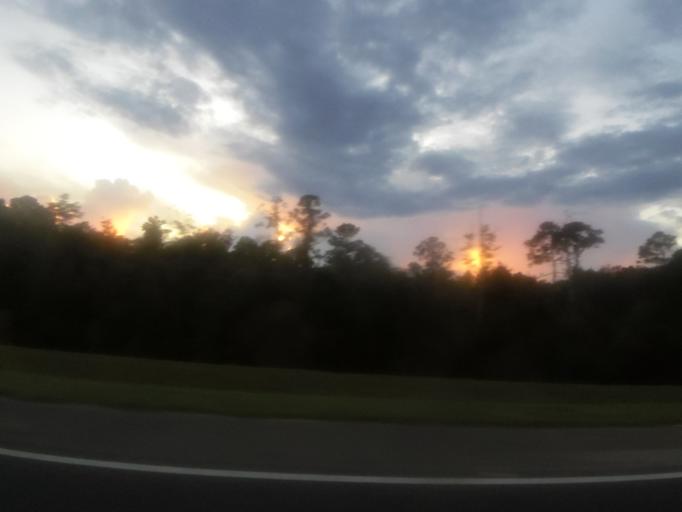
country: US
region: Florida
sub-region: Saint Johns County
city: Palm Valley
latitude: 30.1116
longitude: -81.4501
